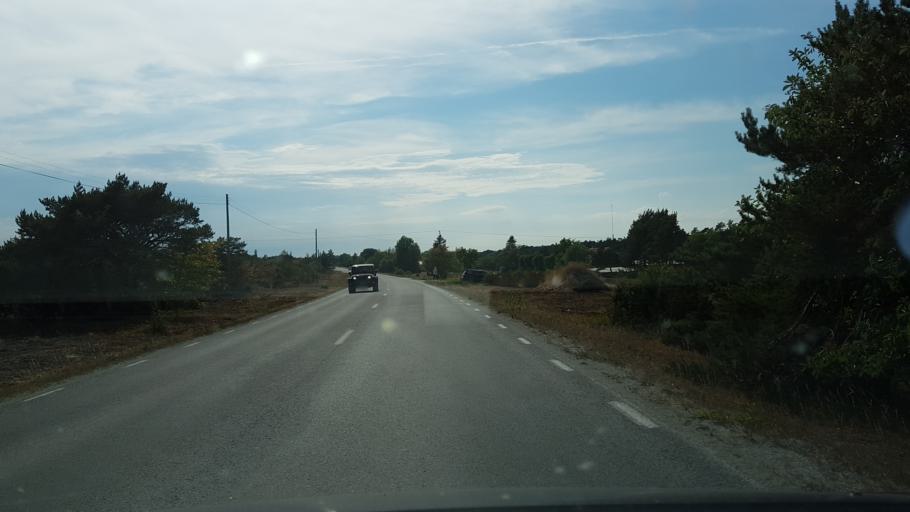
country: SE
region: Gotland
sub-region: Gotland
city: Visby
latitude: 57.6386
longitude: 18.3749
